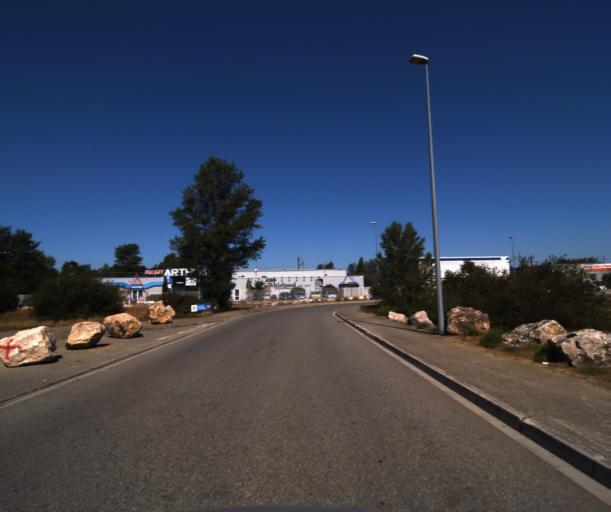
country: FR
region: Midi-Pyrenees
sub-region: Departement de la Haute-Garonne
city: Saubens
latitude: 43.4796
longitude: 1.3328
